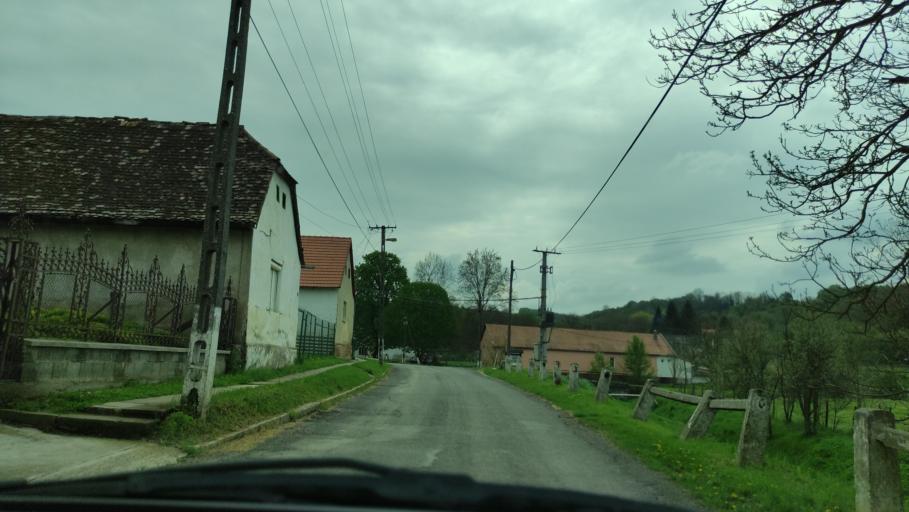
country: HU
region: Baranya
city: Magocs
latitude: 46.2962
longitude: 18.2023
